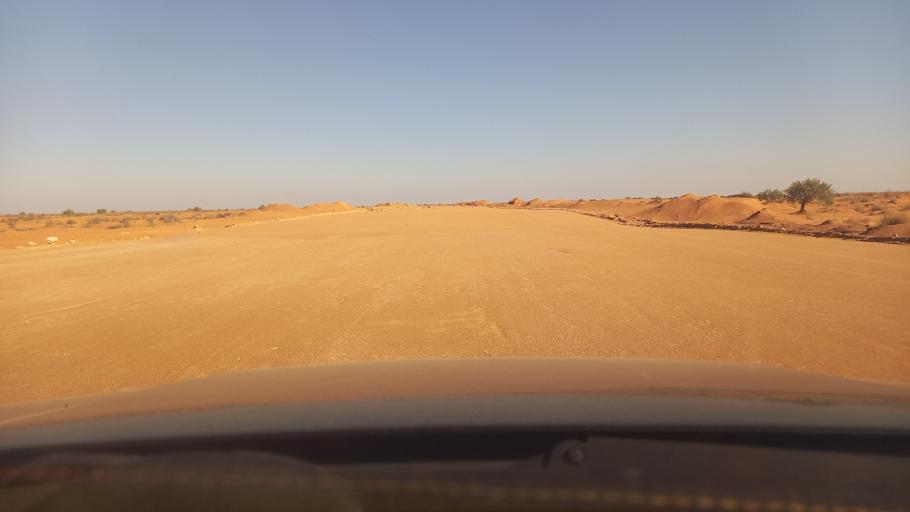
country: TN
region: Madanin
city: Medenine
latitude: 33.1596
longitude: 10.5178
